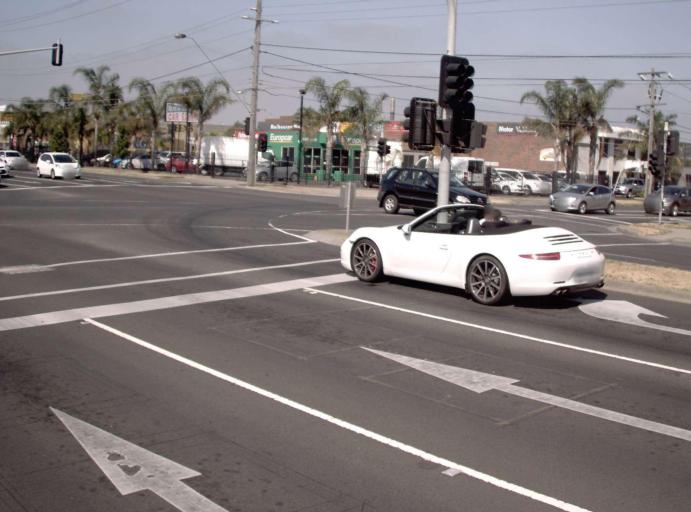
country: AU
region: Victoria
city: Highett
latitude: -37.9497
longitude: 145.0776
